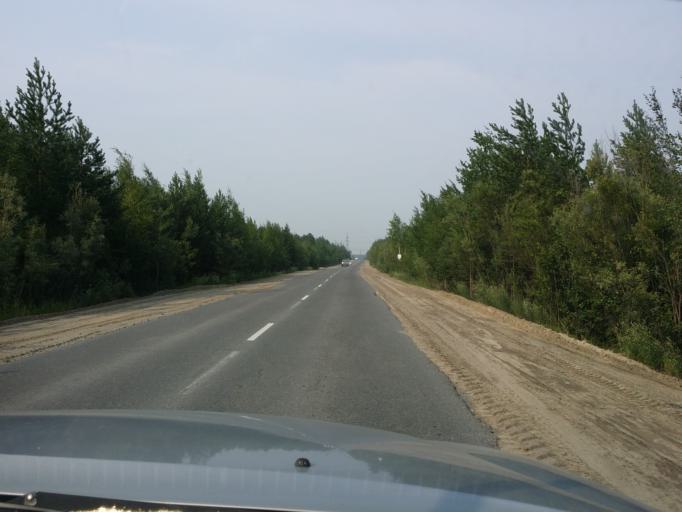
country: RU
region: Khanty-Mansiyskiy Avtonomnyy Okrug
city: Nizhnevartovsk
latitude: 60.9925
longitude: 76.5613
